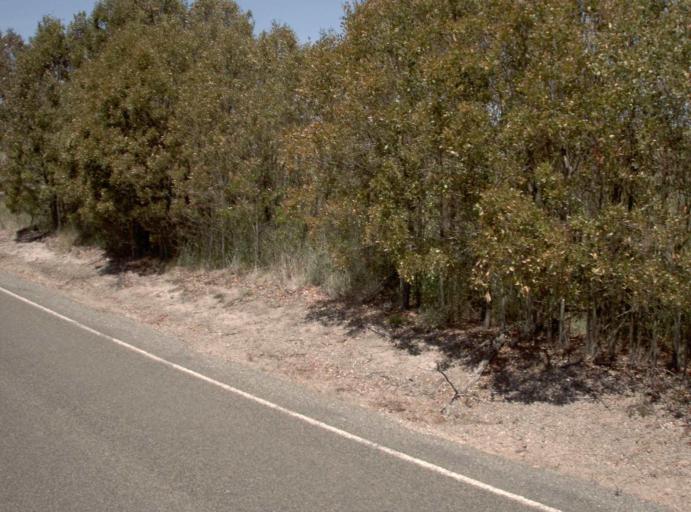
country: AU
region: Victoria
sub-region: Alpine
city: Mount Beauty
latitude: -37.1439
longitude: 147.6473
